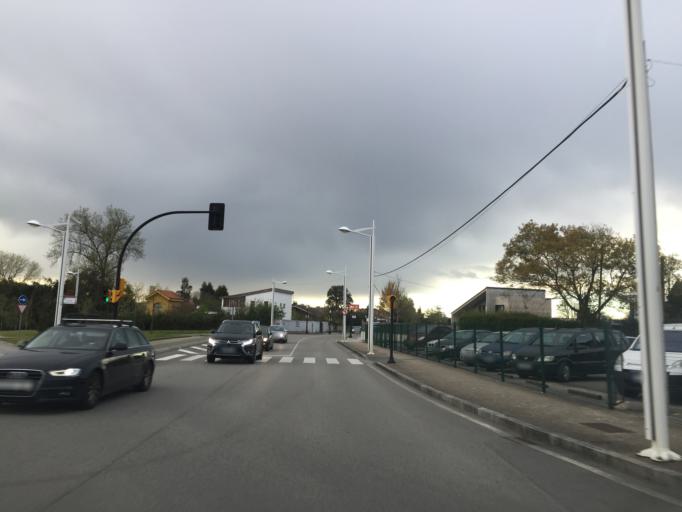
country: ES
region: Asturias
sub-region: Province of Asturias
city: Gijon
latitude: 43.5272
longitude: -5.6286
